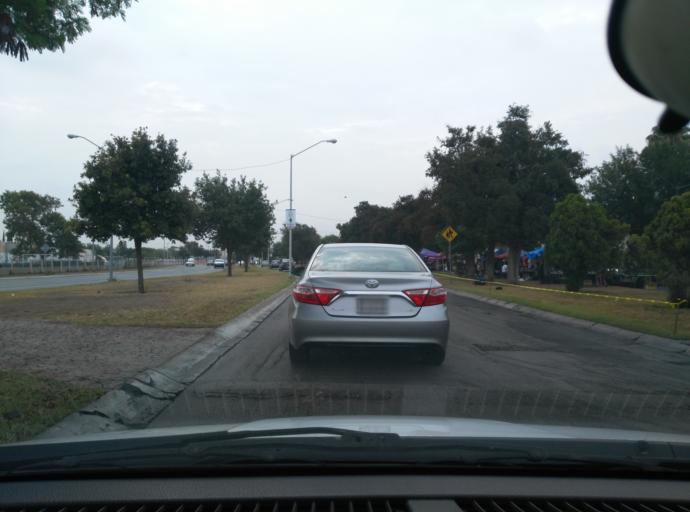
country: MX
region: Nuevo Leon
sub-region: Apodaca
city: Fraccionamiento Cosmopolis Octavo Sector
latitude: 25.7718
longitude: -100.2551
